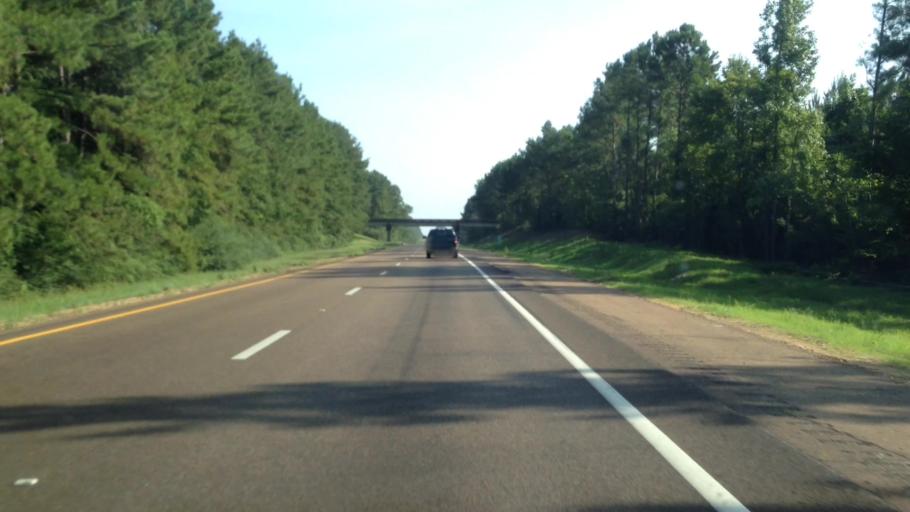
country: US
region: Mississippi
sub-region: Lincoln County
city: Brookhaven
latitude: 31.4477
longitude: -90.4792
